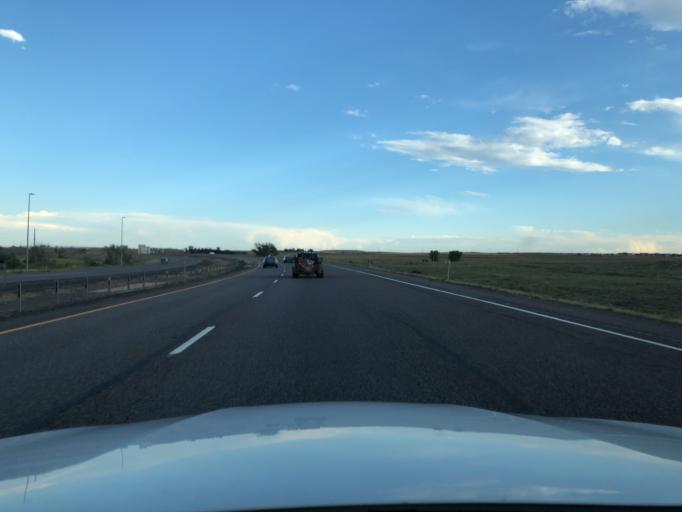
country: US
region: Colorado
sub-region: Adams County
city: Brighton
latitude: 39.9104
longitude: -104.7792
